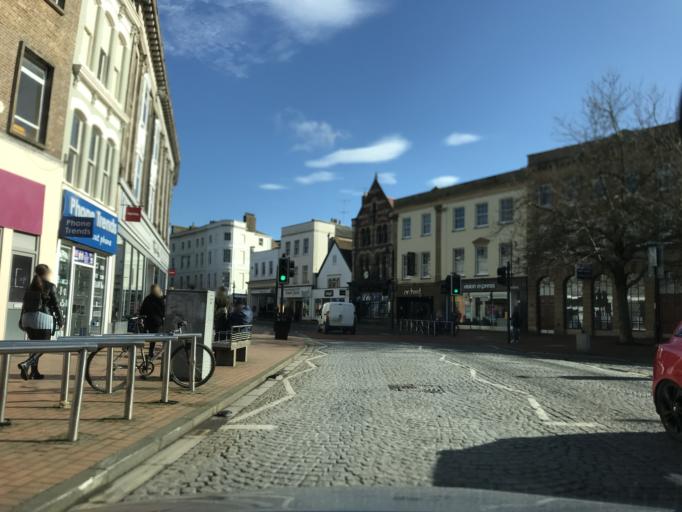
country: GB
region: England
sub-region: Somerset
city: Taunton
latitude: 51.0147
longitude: -3.1025
